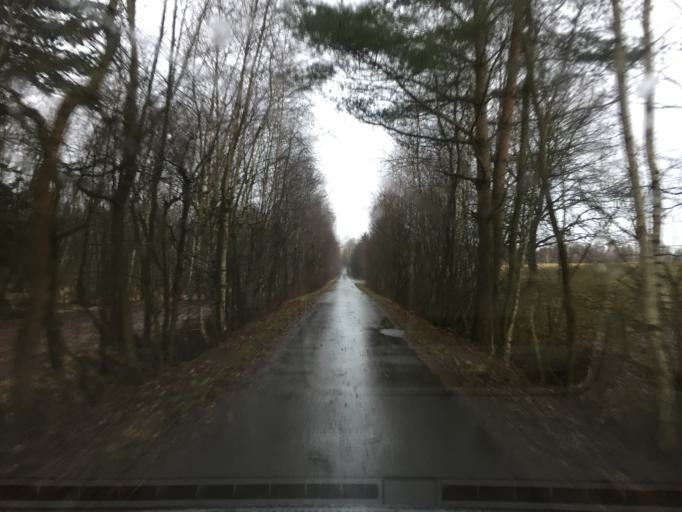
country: DE
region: Lower Saxony
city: Maasen
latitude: 52.6521
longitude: 8.8668
